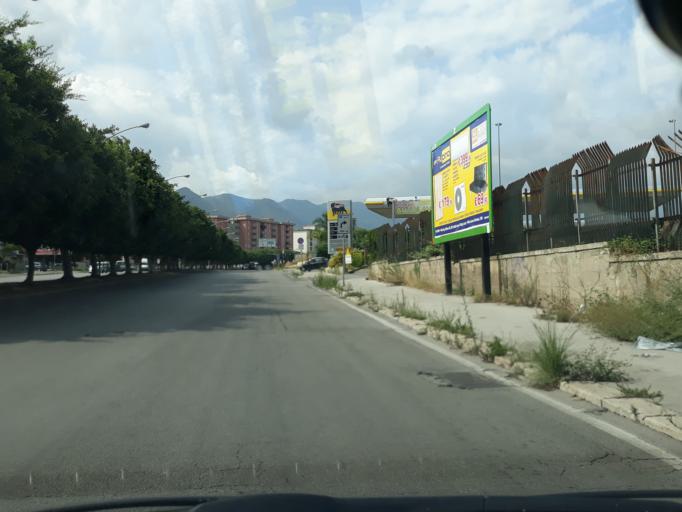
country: IT
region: Sicily
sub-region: Palermo
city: Palermo
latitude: 38.1004
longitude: 13.3471
